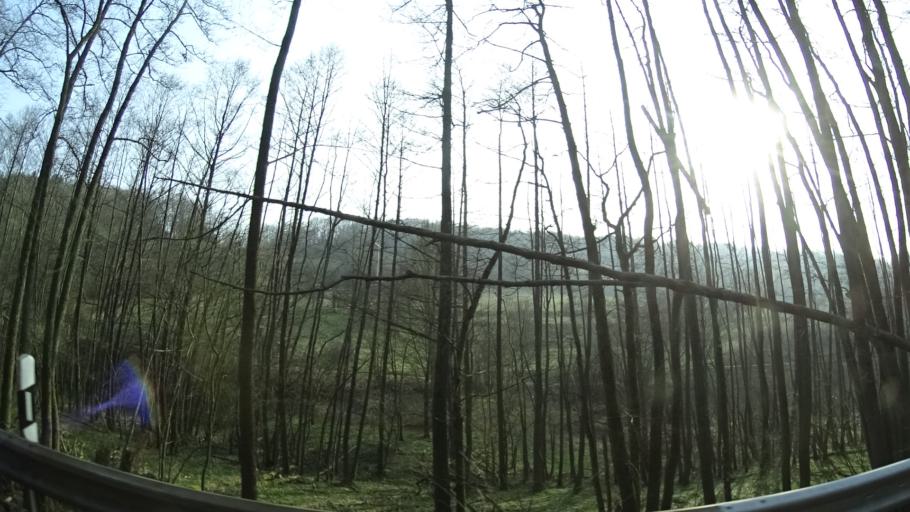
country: DE
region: Rheinland-Pfalz
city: Fockelberg
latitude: 49.5440
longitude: 7.4906
